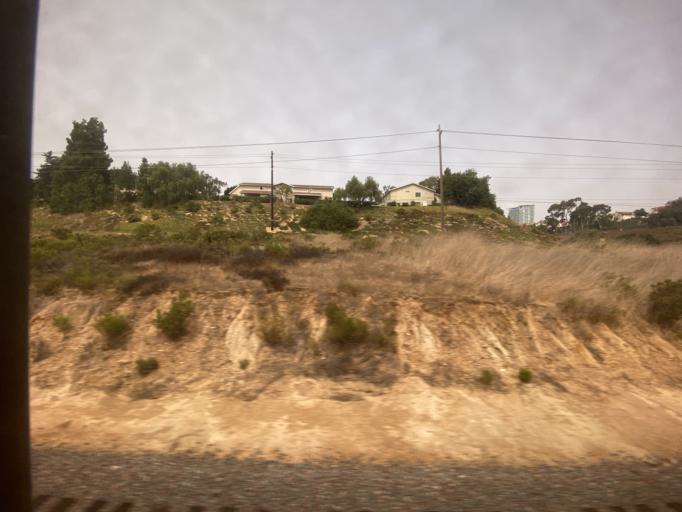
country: US
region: California
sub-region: San Diego County
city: La Jolla
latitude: 32.8610
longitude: -117.2128
